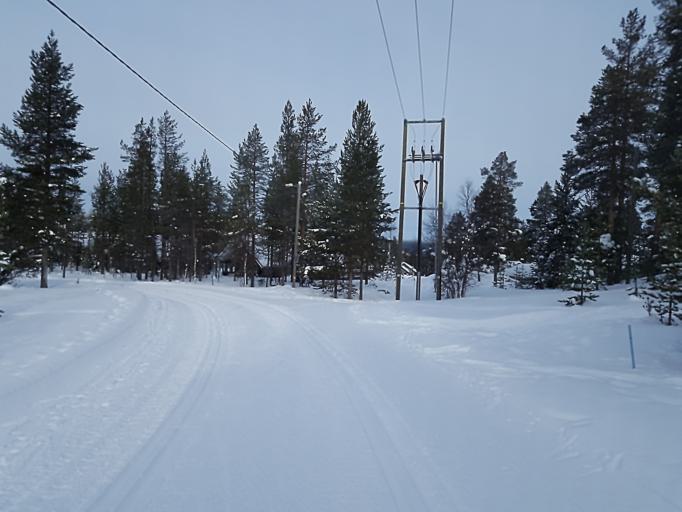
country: FI
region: Lapland
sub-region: Tunturi-Lappi
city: Kolari
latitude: 67.5965
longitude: 24.1586
